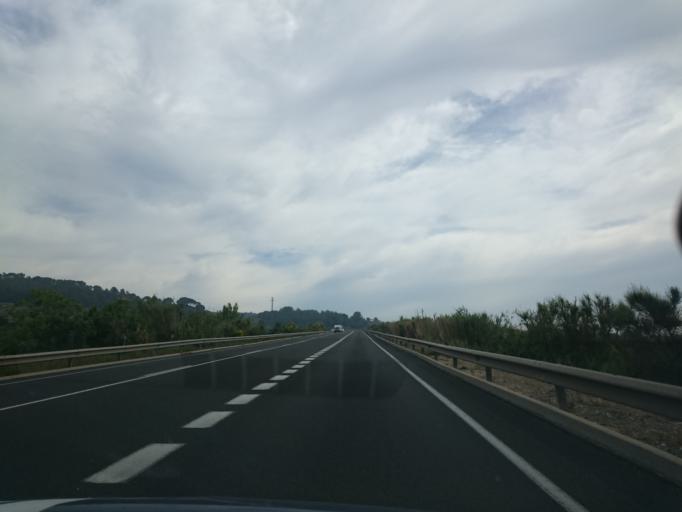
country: ES
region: Catalonia
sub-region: Provincia de Barcelona
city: Sant Pere de Riudebitlles
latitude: 41.4577
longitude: 1.6923
